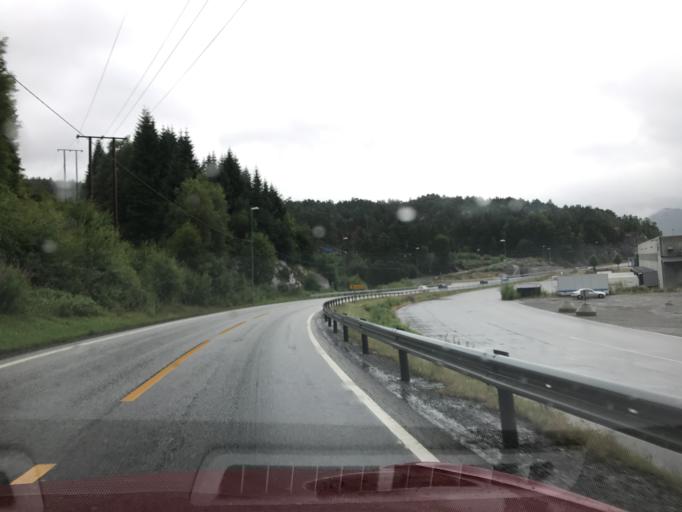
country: NO
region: Vest-Agder
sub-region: Flekkefjord
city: Flekkefjord
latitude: 58.2818
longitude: 6.7031
